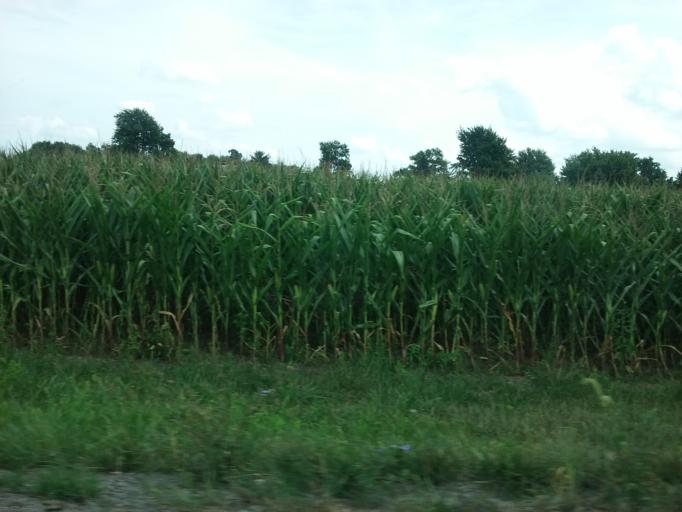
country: US
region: Ohio
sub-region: Hancock County
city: Findlay
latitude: 41.0407
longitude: -83.6887
